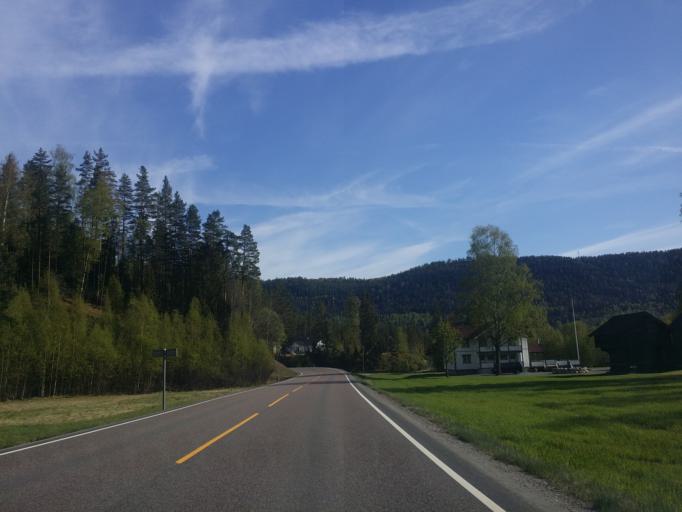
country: NO
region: Telemark
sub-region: Hjartdal
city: Sauland
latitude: 59.6080
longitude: 9.0214
